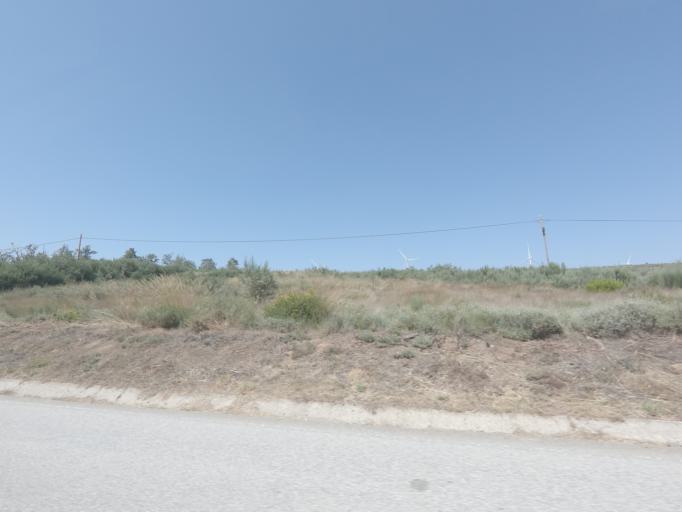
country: PT
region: Viseu
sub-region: Tarouca
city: Tarouca
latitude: 40.9878
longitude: -7.8072
